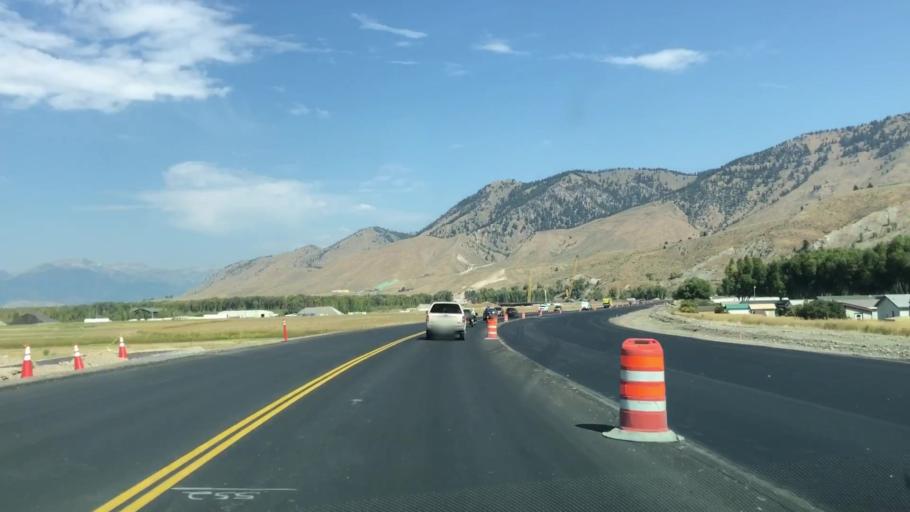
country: US
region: Wyoming
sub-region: Teton County
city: South Park
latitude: 43.3752
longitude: -110.7448
